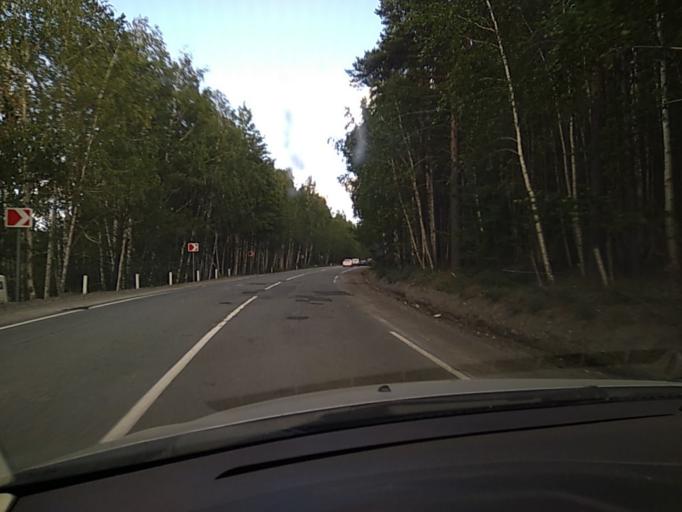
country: RU
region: Chelyabinsk
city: Karabash
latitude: 55.5030
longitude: 60.2719
